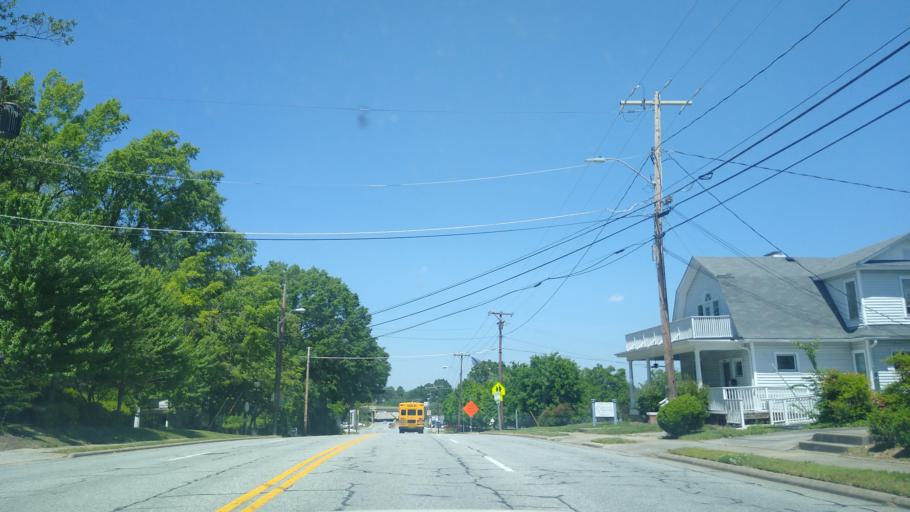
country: US
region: North Carolina
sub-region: Guilford County
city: Greensboro
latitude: 36.0837
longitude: -79.7829
